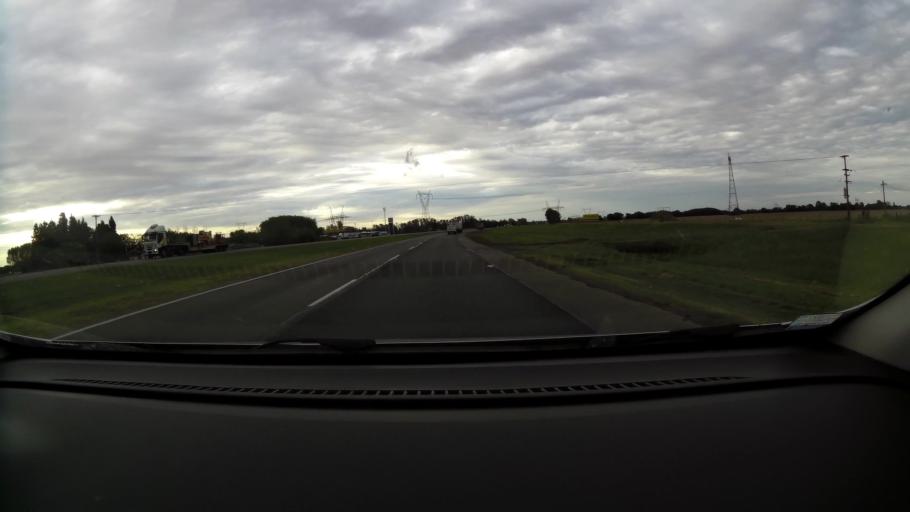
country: AR
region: Buenos Aires
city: San Nicolas de los Arroyos
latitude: -33.4315
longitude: -60.1744
